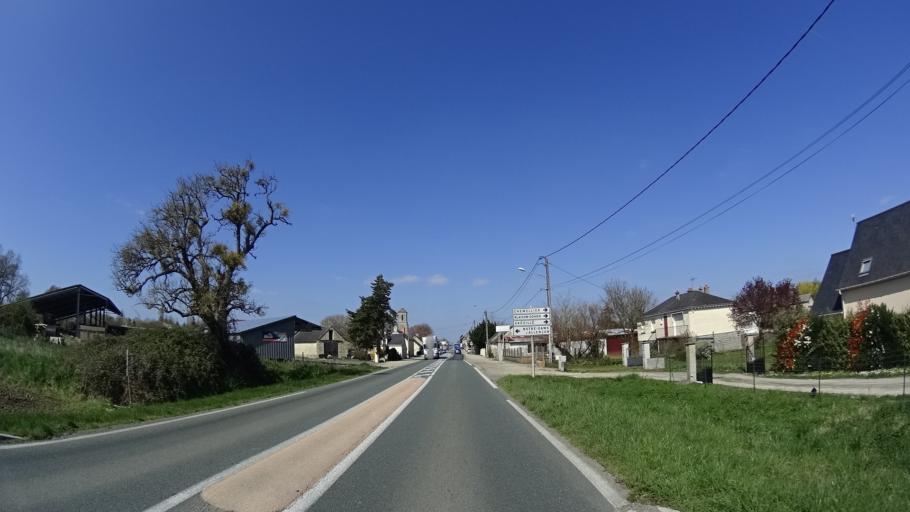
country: FR
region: Pays de la Loire
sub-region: Departement de Maine-et-Loire
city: Brissac-Quince
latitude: 47.3167
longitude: -0.4061
